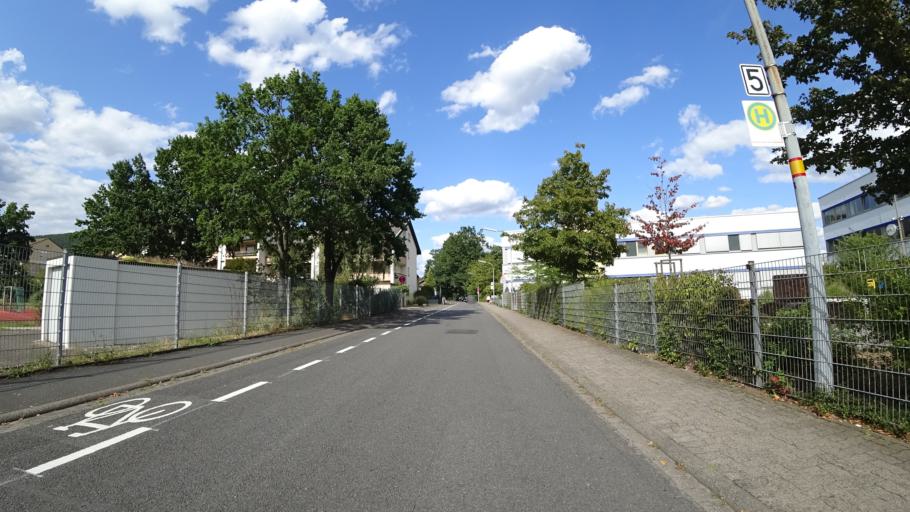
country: DE
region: Bavaria
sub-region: Regierungsbezirk Unterfranken
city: Miltenberg
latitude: 49.7080
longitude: 9.2514
